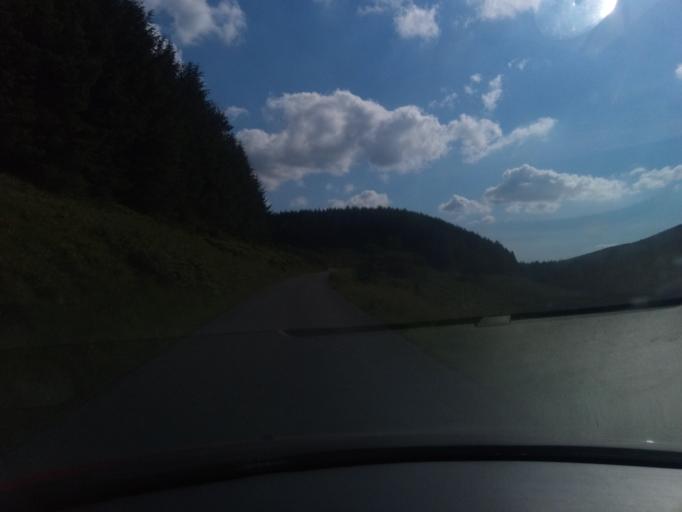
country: GB
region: Scotland
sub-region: The Scottish Borders
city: Innerleithen
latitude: 55.4712
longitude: -3.1458
